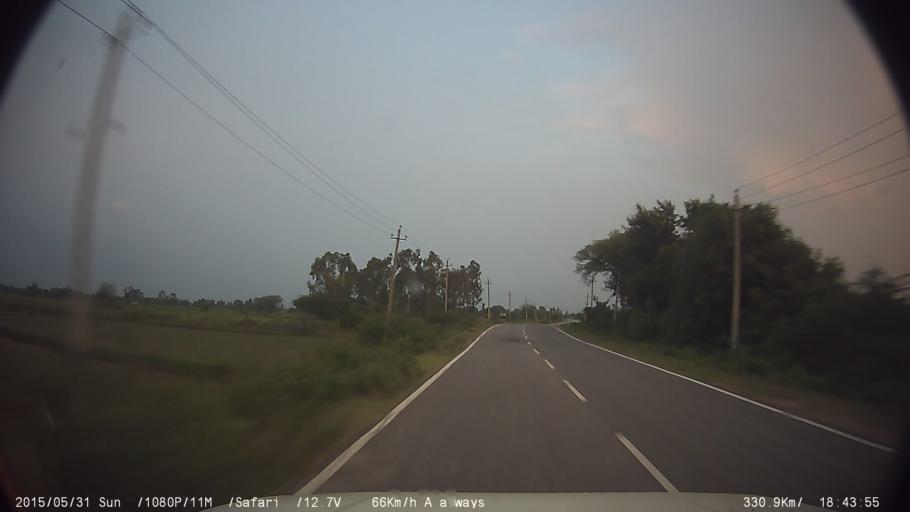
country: IN
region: Karnataka
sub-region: Mysore
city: Tirumakudal Narsipur
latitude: 12.1566
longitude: 76.8110
